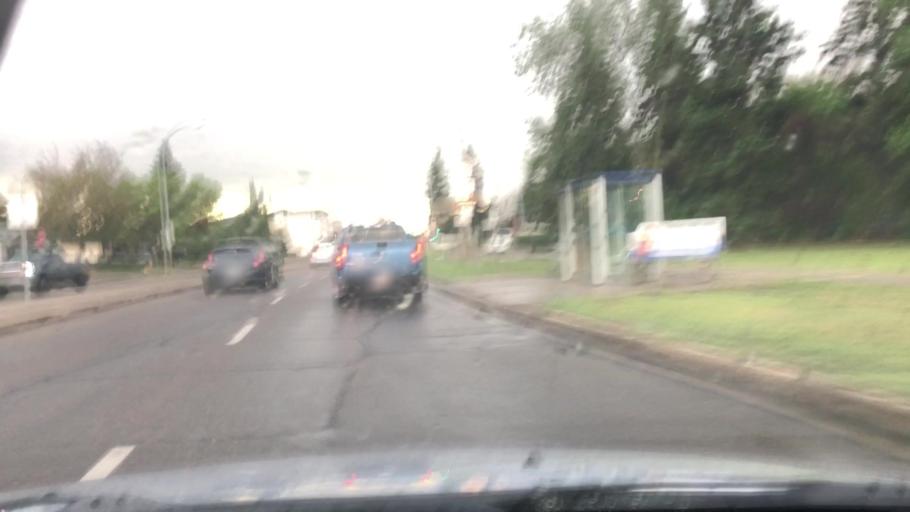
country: CA
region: Alberta
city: Edmonton
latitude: 53.5987
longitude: -113.5416
